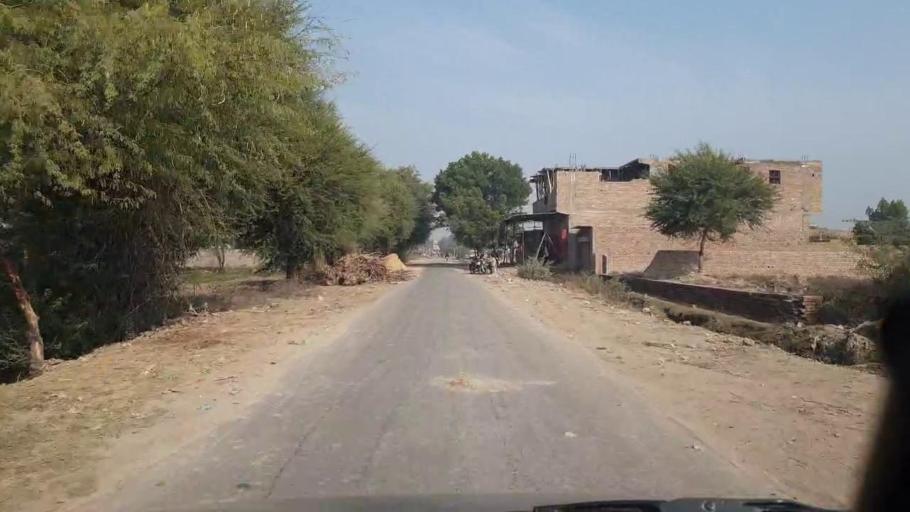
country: PK
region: Sindh
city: Shahdadpur
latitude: 26.0236
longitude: 68.5463
